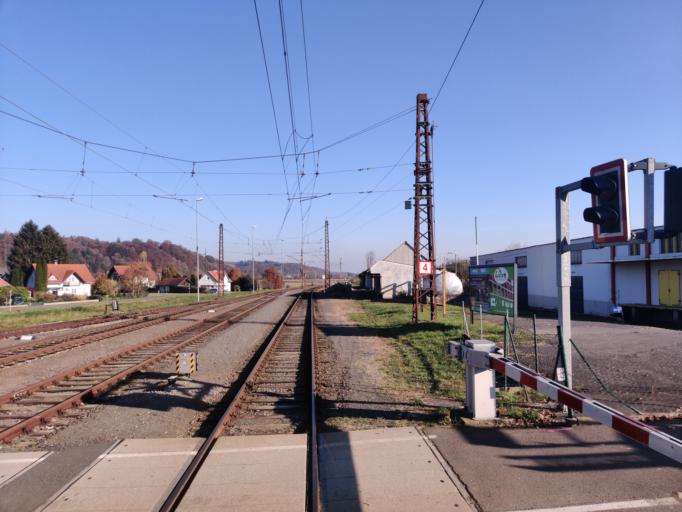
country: AT
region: Styria
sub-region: Politischer Bezirk Suedoststeiermark
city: Feldbach
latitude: 46.9585
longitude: 15.8930
